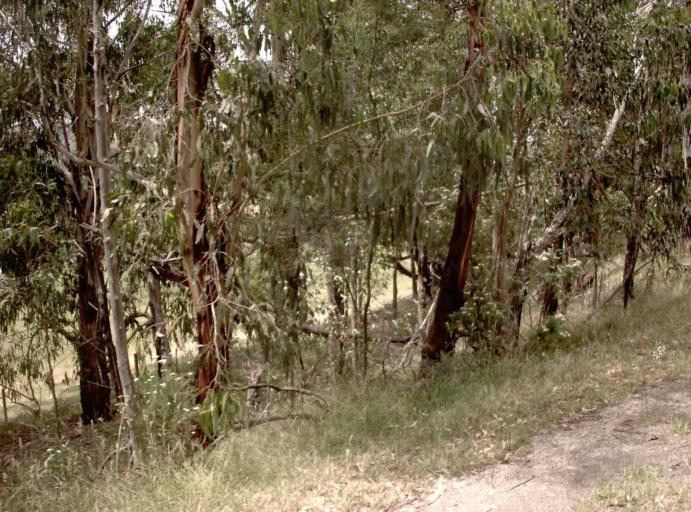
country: AU
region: Victoria
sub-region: Latrobe
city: Traralgon
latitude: -38.4436
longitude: 146.7335
